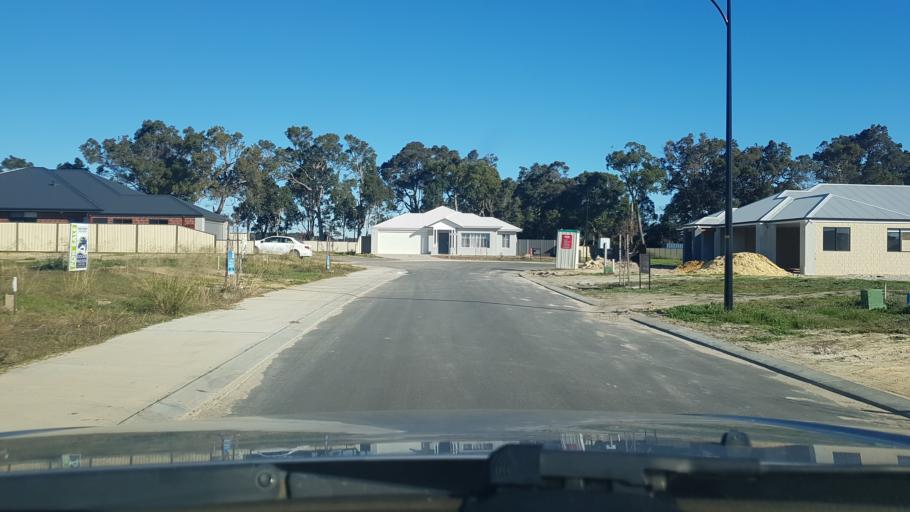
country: AU
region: Western Australia
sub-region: Augusta-Margaret River Shire
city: Margaret River
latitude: -33.8571
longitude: 115.1021
